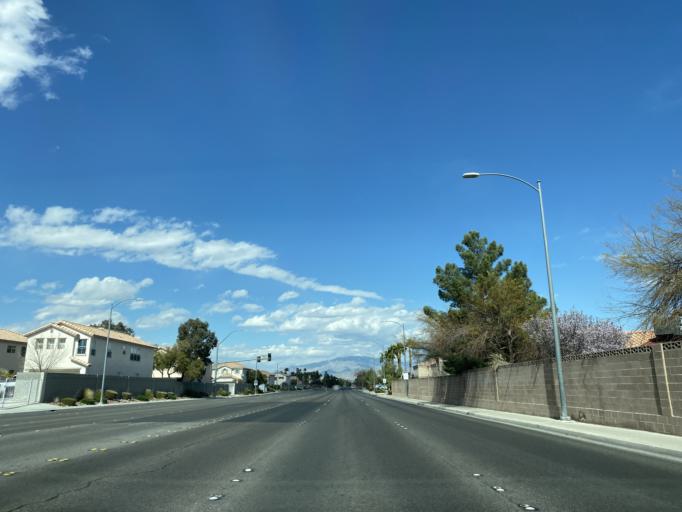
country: US
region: Nevada
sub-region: Clark County
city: Spring Valley
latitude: 36.2294
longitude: -115.2606
